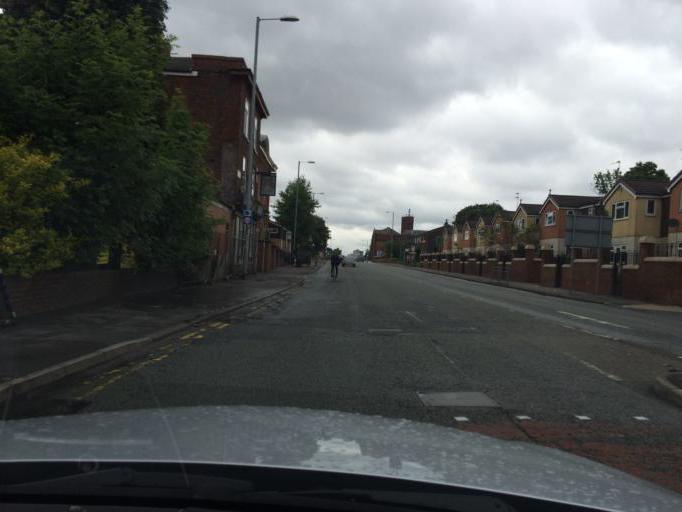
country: GB
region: England
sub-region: Manchester
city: Longsight
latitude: 53.4599
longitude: -2.2046
